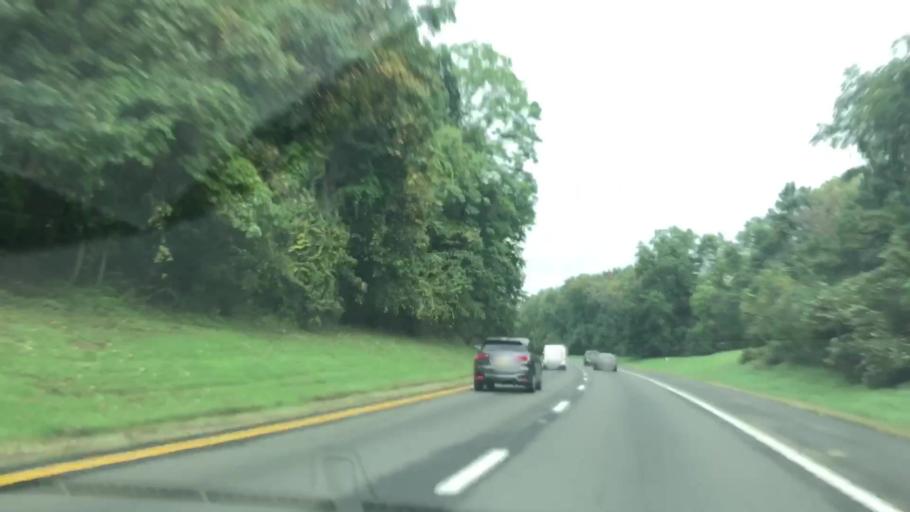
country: US
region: New Jersey
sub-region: Bergen County
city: Woodcliff Lake
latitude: 41.0307
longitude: -74.0688
